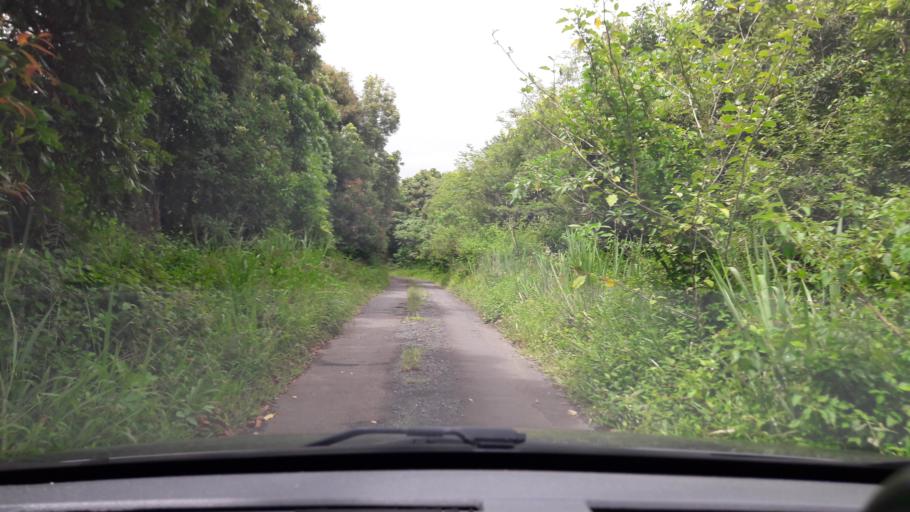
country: RE
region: Reunion
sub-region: Reunion
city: Saint-Benoit
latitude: -21.0985
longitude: 55.6970
